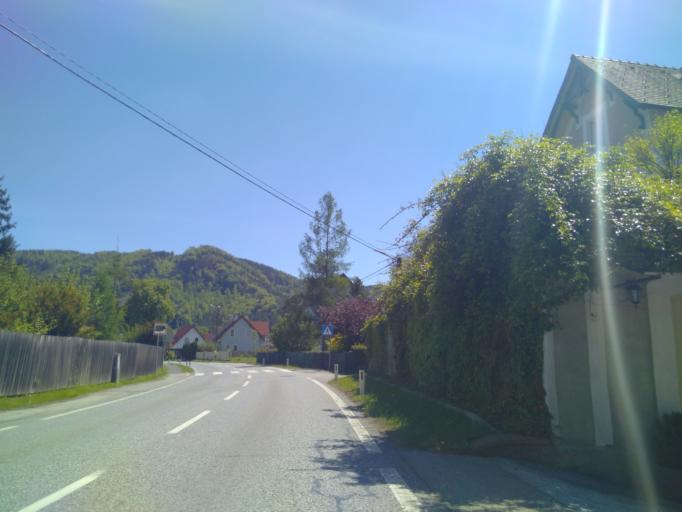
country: AT
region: Styria
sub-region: Politischer Bezirk Graz-Umgebung
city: Gratkorn
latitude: 47.1203
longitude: 15.3364
